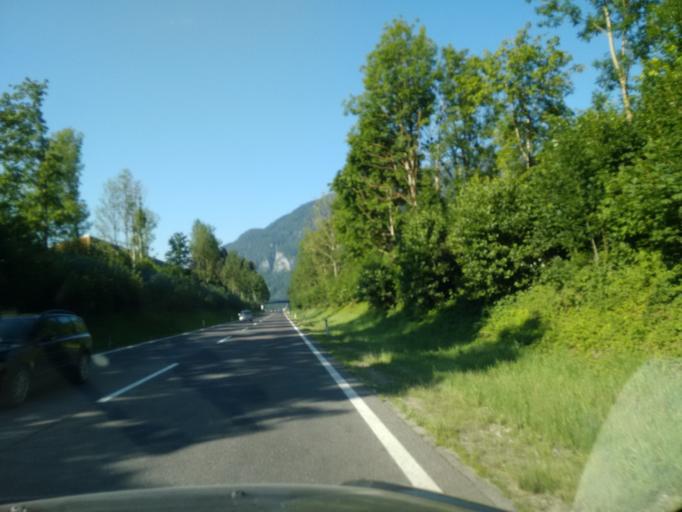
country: AT
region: Upper Austria
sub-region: Politischer Bezirk Gmunden
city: Bad Ischl
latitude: 47.7048
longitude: 13.6270
